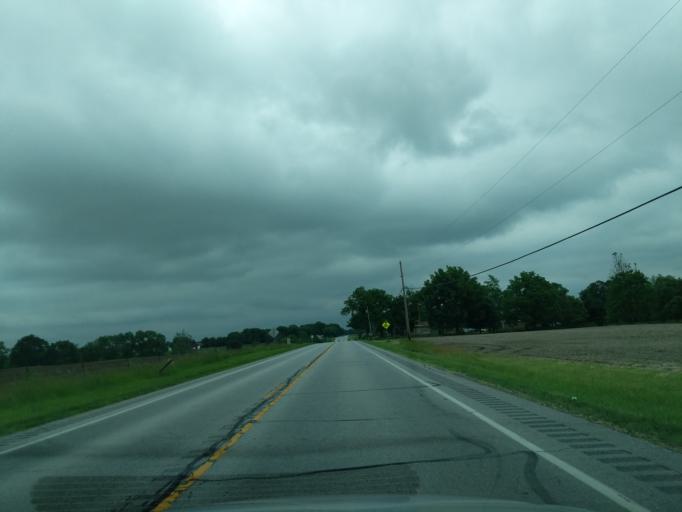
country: US
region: Indiana
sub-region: Madison County
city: Alexandria
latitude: 40.2775
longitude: -85.7171
